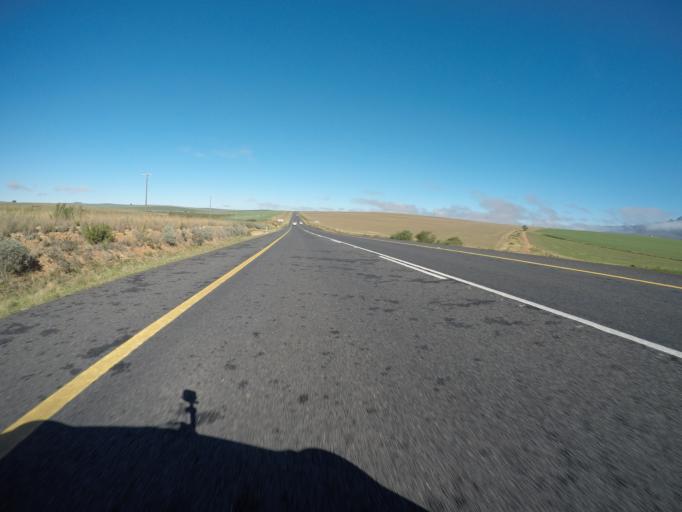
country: ZA
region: Western Cape
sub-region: Cape Winelands District Municipality
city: Ashton
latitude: -34.0929
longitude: 20.0800
